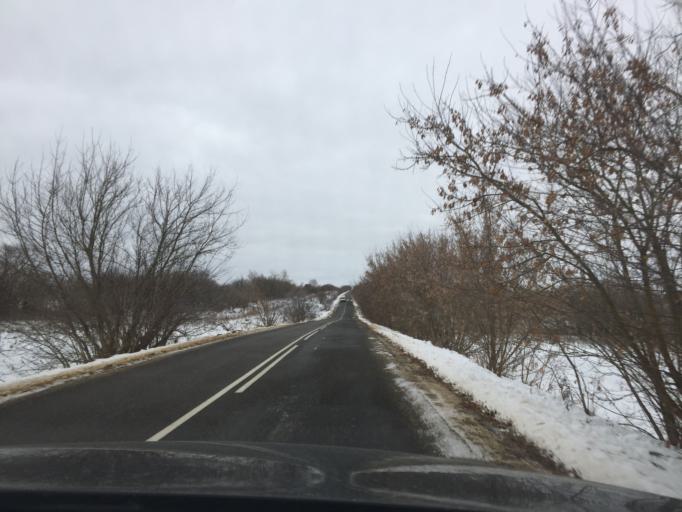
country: RU
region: Tula
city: Teploye
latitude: 53.7905
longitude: 37.6102
